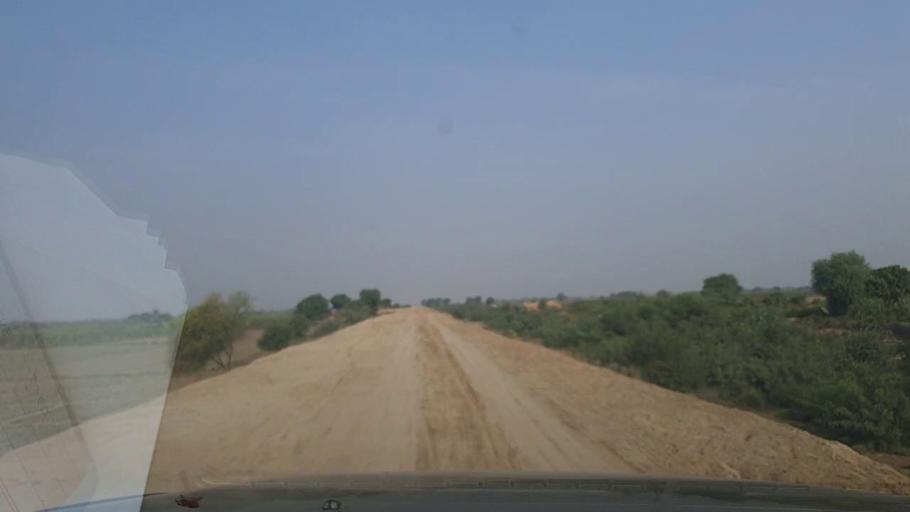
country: PK
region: Sindh
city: Bulri
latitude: 24.9905
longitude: 68.2927
